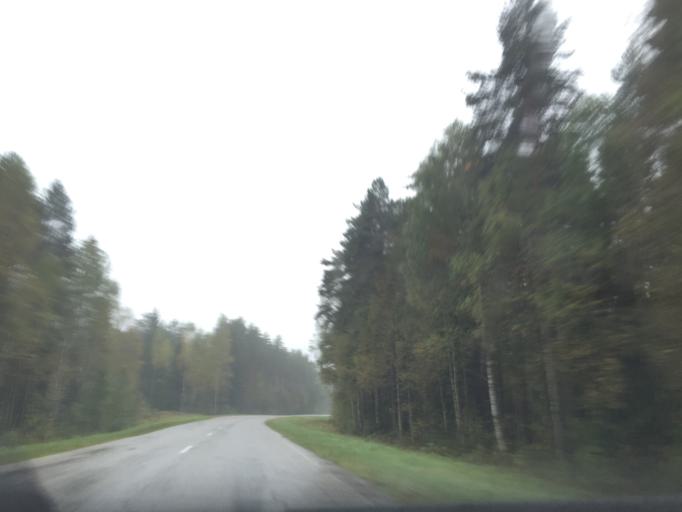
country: LV
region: Ropazu
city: Ropazi
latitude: 57.0009
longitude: 24.6694
